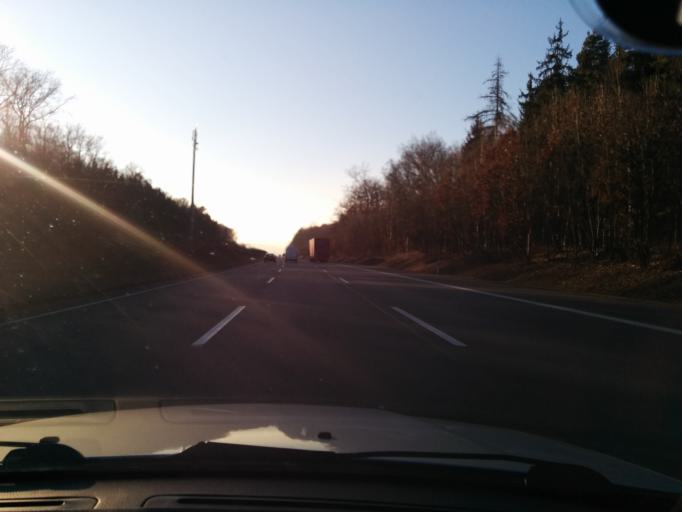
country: DE
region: Thuringia
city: Emleben
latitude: 50.9085
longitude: 10.6522
